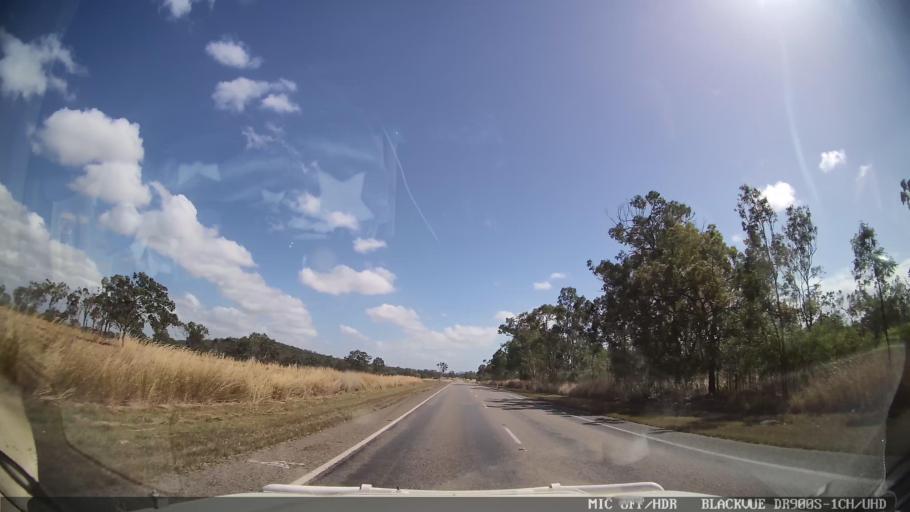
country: AU
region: Queensland
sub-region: Whitsunday
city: Red Hill
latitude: -20.1847
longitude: 148.3549
